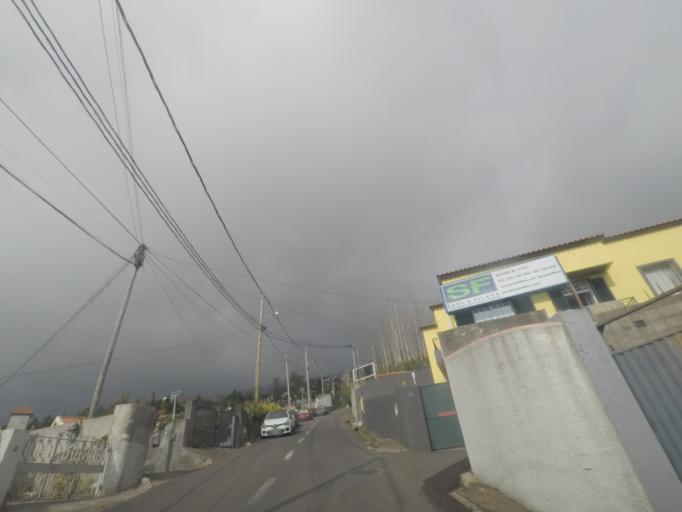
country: PT
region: Madeira
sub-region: Funchal
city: Nossa Senhora do Monte
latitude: 32.6718
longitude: -16.8991
